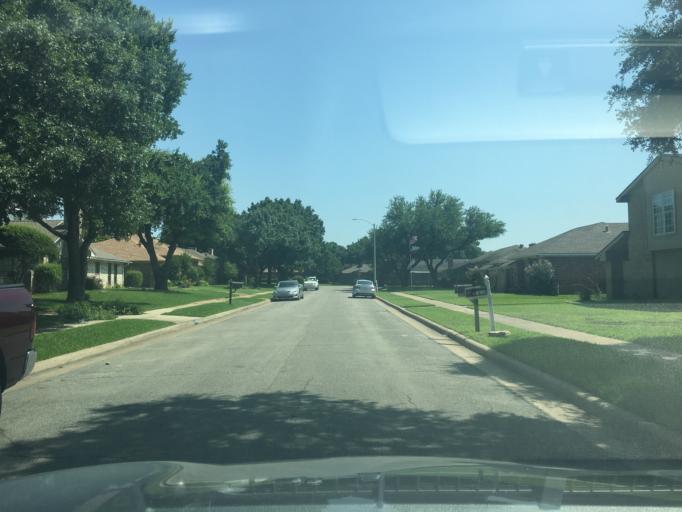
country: US
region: Texas
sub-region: Dallas County
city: Richardson
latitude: 32.9288
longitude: -96.7062
